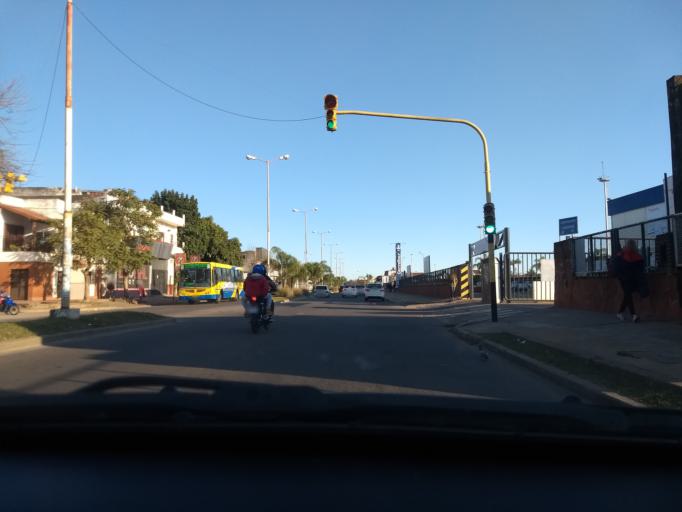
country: AR
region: Corrientes
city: Corrientes
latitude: -27.4766
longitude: -58.8142
